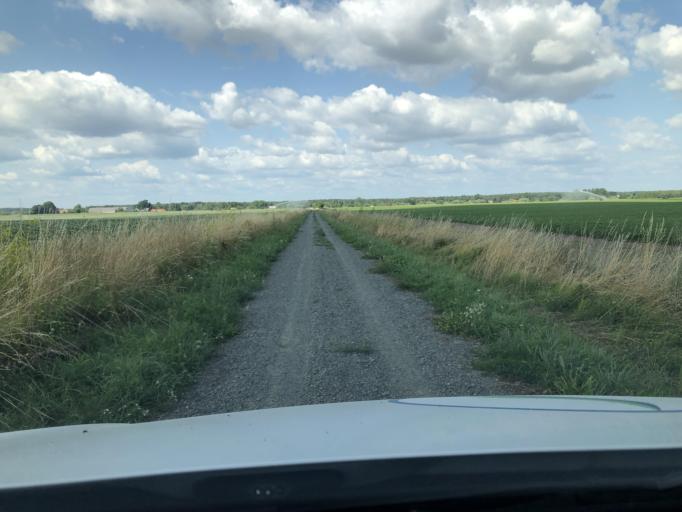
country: SE
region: Skane
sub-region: Kristianstads Kommun
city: Degeberga
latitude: 55.8871
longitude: 14.0813
